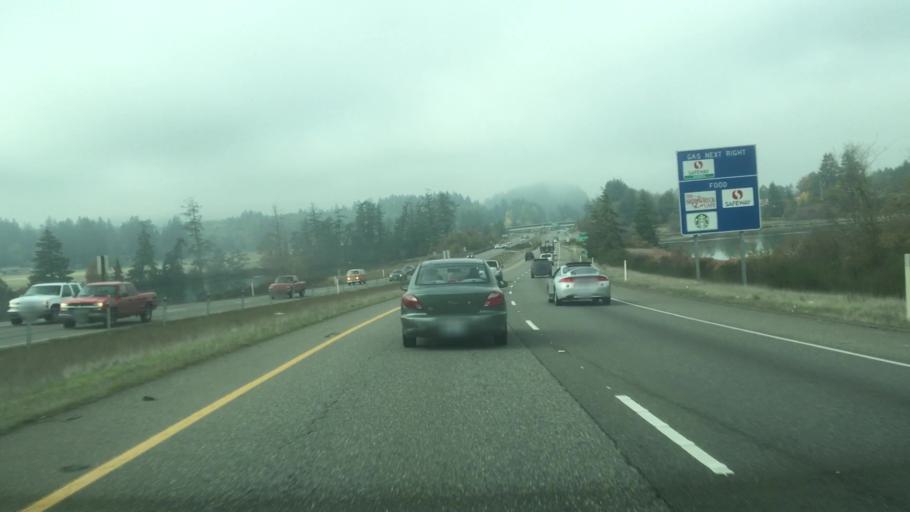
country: US
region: Washington
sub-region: Thurston County
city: Tumwater
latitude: 47.0430
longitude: -122.9870
